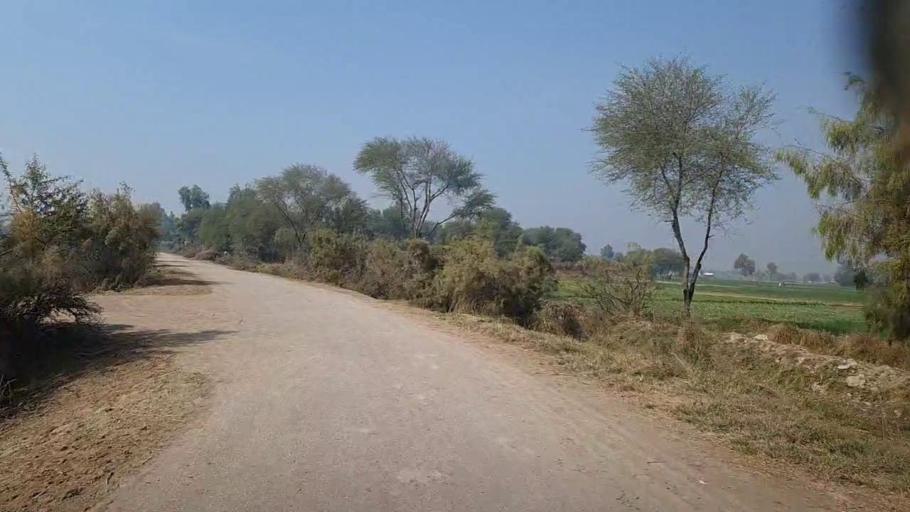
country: PK
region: Sindh
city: Khairpur
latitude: 27.9647
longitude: 69.6662
